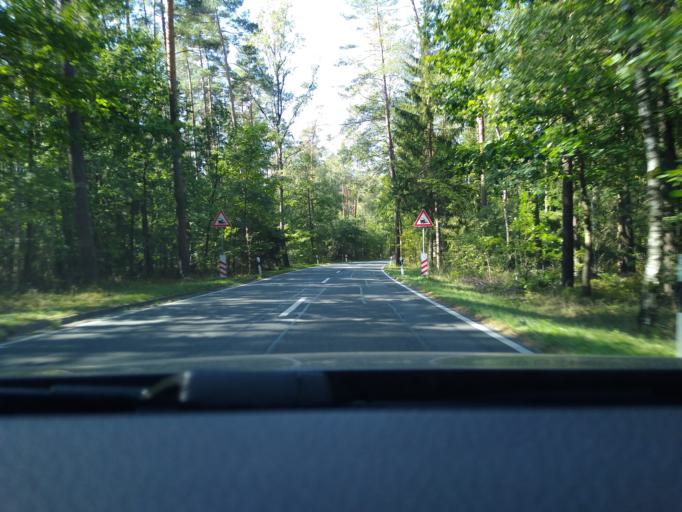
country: DE
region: Bavaria
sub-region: Regierungsbezirk Mittelfranken
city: Seukendorf
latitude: 49.4639
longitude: 10.9181
